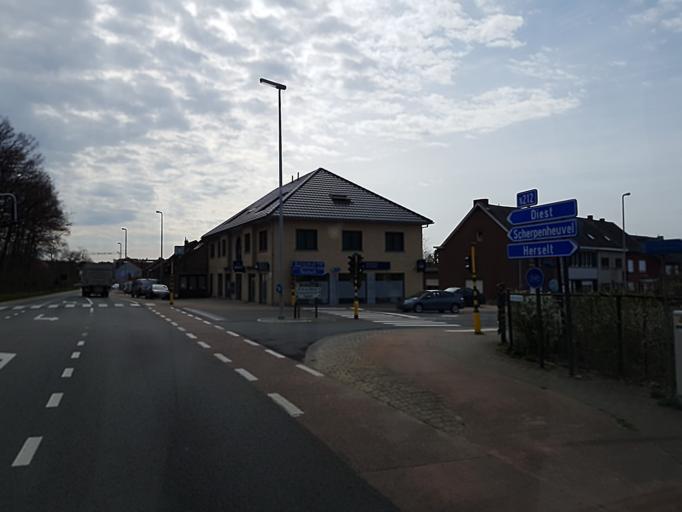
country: BE
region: Flanders
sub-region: Provincie Vlaams-Brabant
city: Scherpenheuvel-Zichem
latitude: 51.0307
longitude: 4.9772
